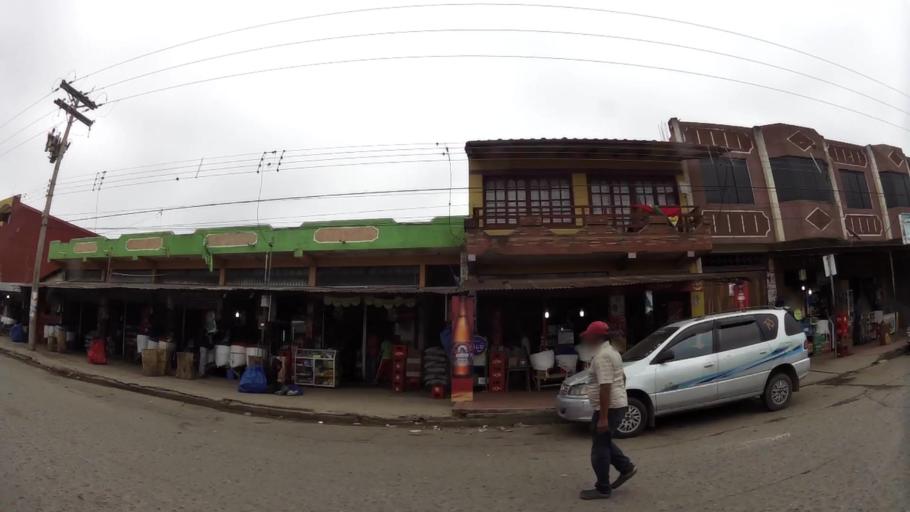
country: BO
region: Santa Cruz
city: Santa Cruz de la Sierra
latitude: -17.8284
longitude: -63.2025
